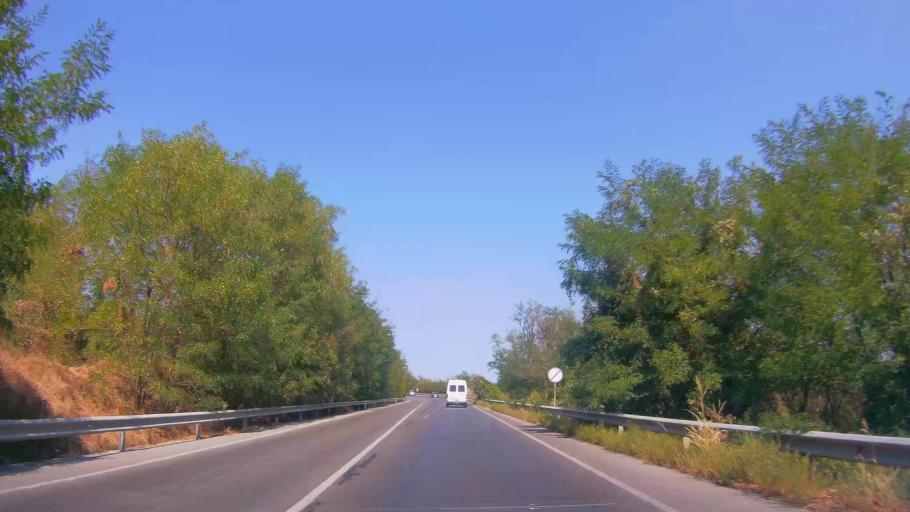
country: BG
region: Razgrad
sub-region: Obshtina Tsar Kaloyan
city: Tsar Kaloyan
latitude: 43.6238
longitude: 26.2125
